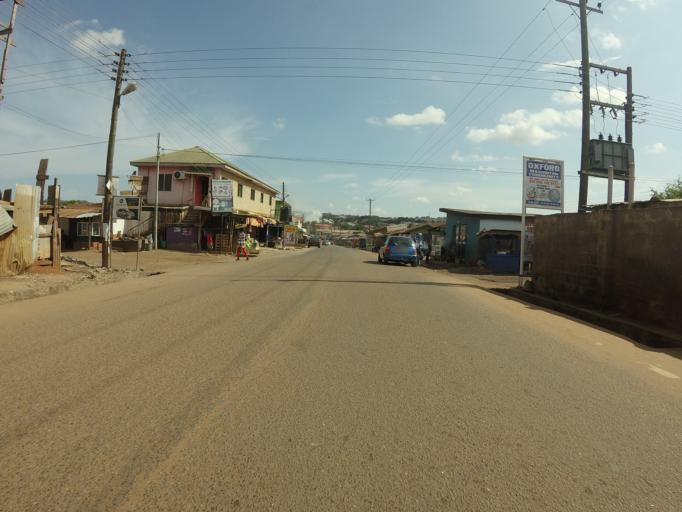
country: GH
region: Greater Accra
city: Medina Estates
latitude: 5.6756
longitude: -0.1818
